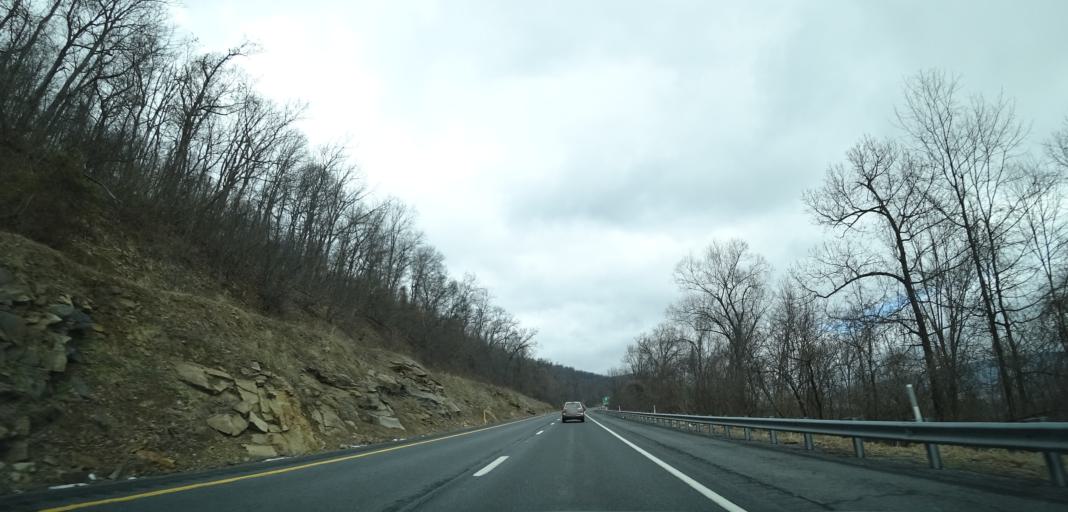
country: US
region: Pennsylvania
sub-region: Bedford County
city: Earlston
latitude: 39.8602
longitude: -78.2654
